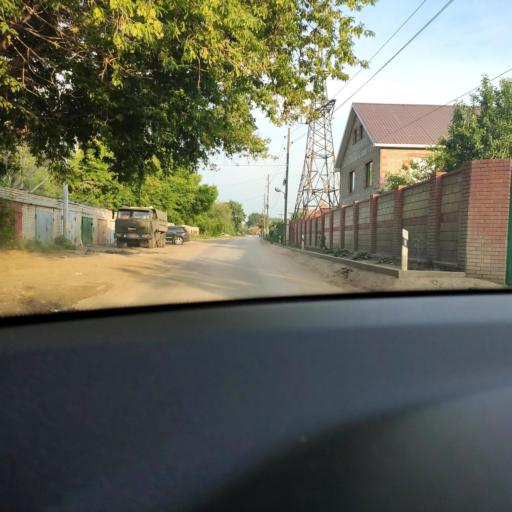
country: RU
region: Samara
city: Rozhdestveno
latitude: 53.1490
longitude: 50.0252
